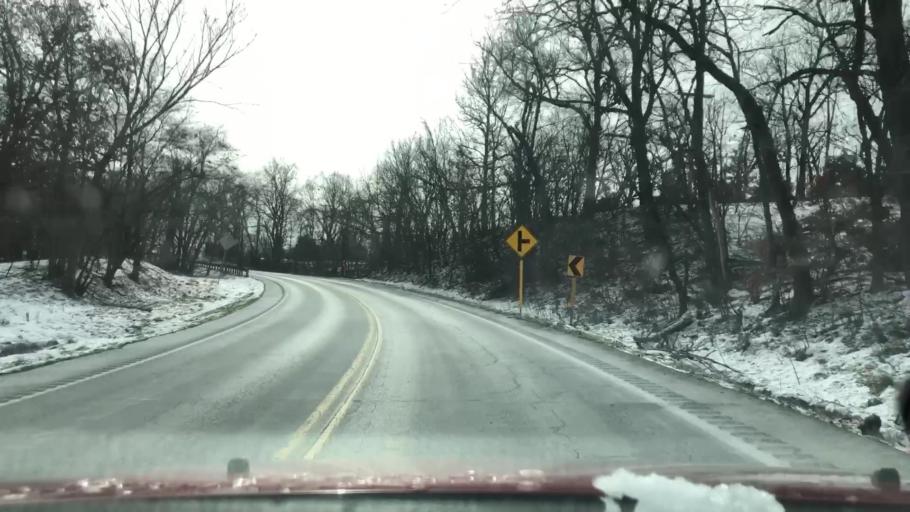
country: US
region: Missouri
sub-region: Jackson County
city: Oak Grove
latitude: 38.9359
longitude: -94.1335
